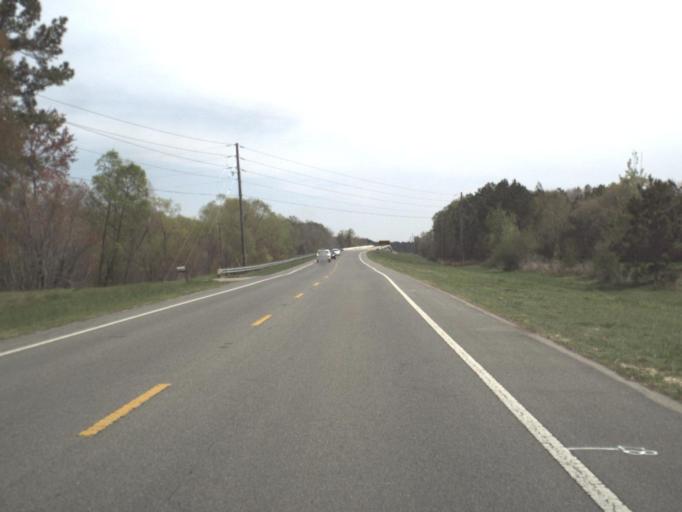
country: US
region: Alabama
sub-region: Geneva County
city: Geneva
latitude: 30.9509
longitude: -85.8524
